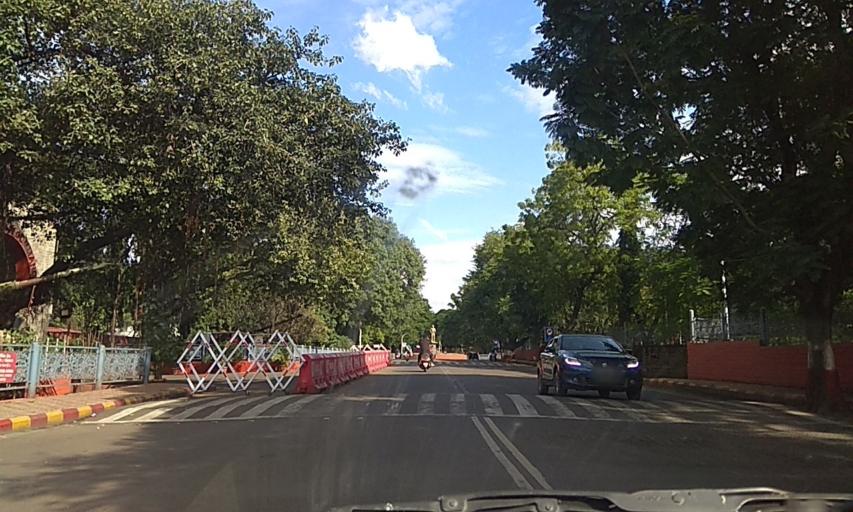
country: IN
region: Maharashtra
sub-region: Pune Division
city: Pune
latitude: 18.5240
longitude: 73.8819
